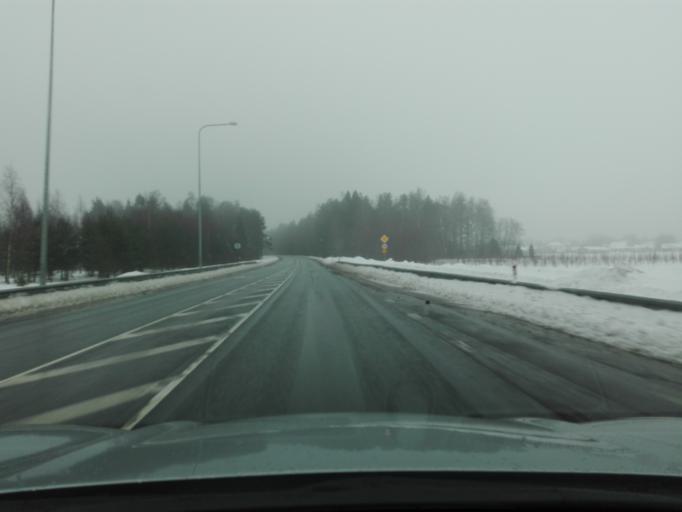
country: EE
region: Raplamaa
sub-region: Kohila vald
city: Kohila
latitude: 59.1690
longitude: 24.7717
